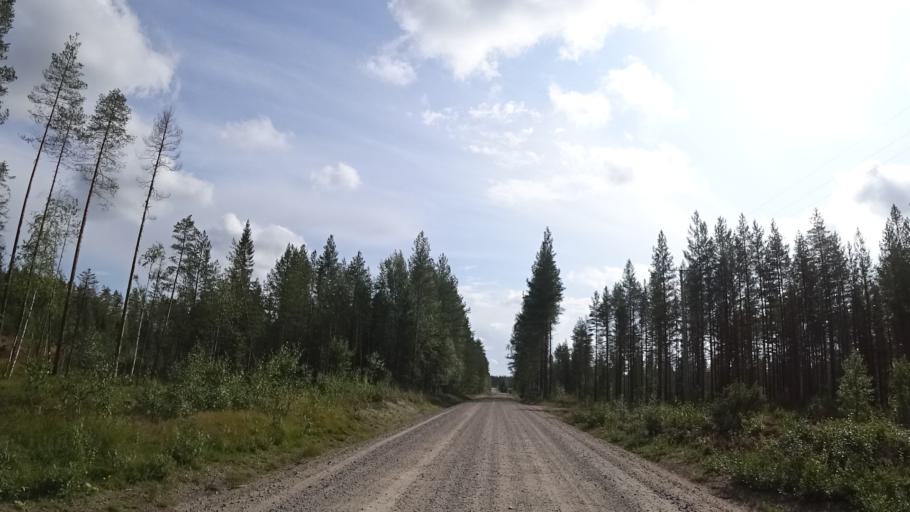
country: FI
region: North Karelia
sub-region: Pielisen Karjala
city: Lieksa
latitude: 63.5533
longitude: 30.0614
